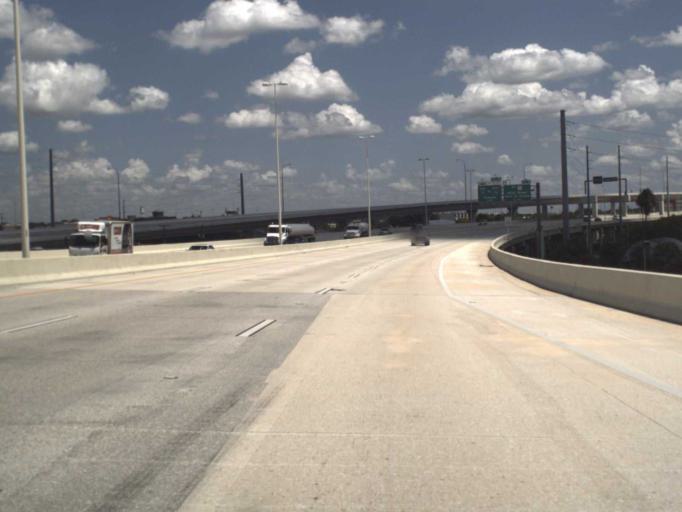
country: US
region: Florida
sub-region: Hillsborough County
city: Tampa
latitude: 27.9539
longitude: -82.4482
